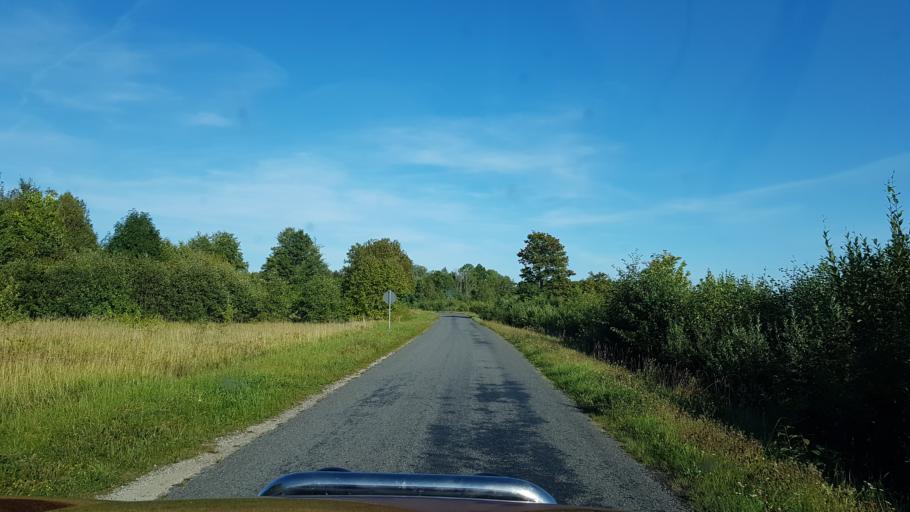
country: LV
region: Salacgrivas
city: Ainazi
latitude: 57.8763
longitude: 24.3680
